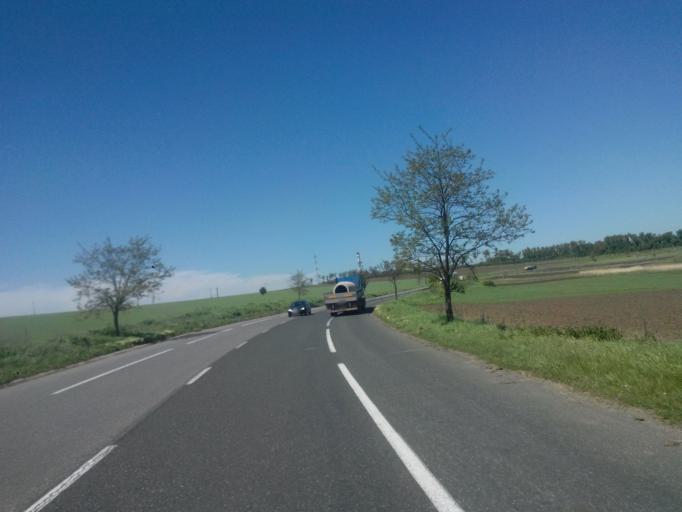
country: RO
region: Iasi
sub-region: Comuna Strunga
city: Strunga
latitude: 47.1529
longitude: 26.9467
